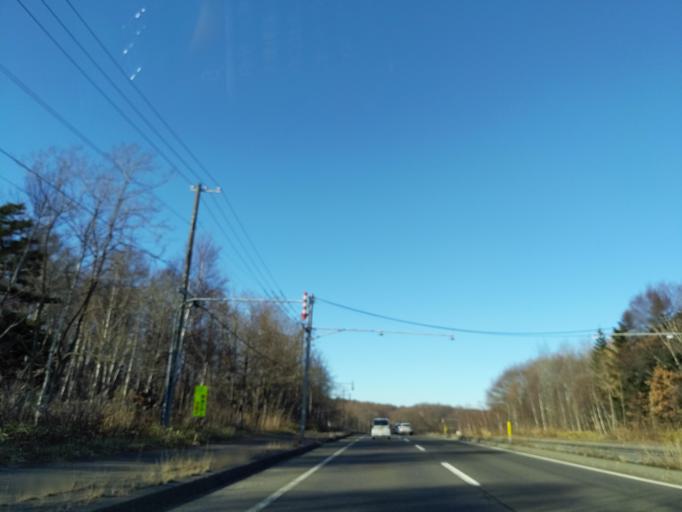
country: JP
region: Hokkaido
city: Kitahiroshima
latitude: 42.9108
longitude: 141.5482
